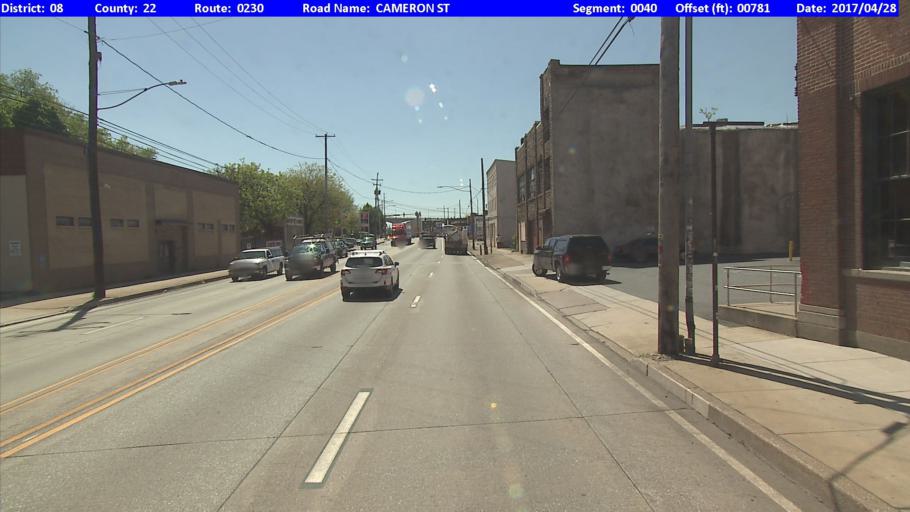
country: US
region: Pennsylvania
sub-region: Dauphin County
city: Harrisburg
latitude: 40.2659
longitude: -76.8751
